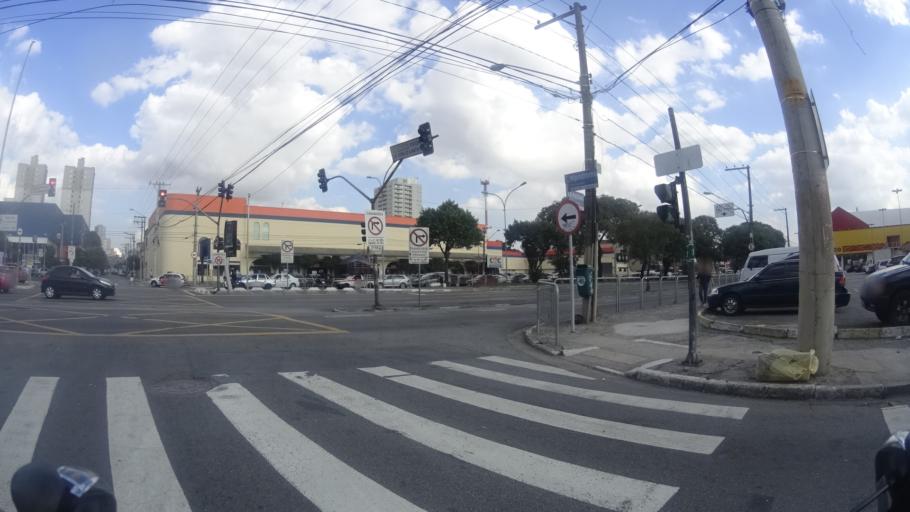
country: BR
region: Sao Paulo
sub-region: Sao Paulo
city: Sao Paulo
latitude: -23.5494
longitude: -46.6055
